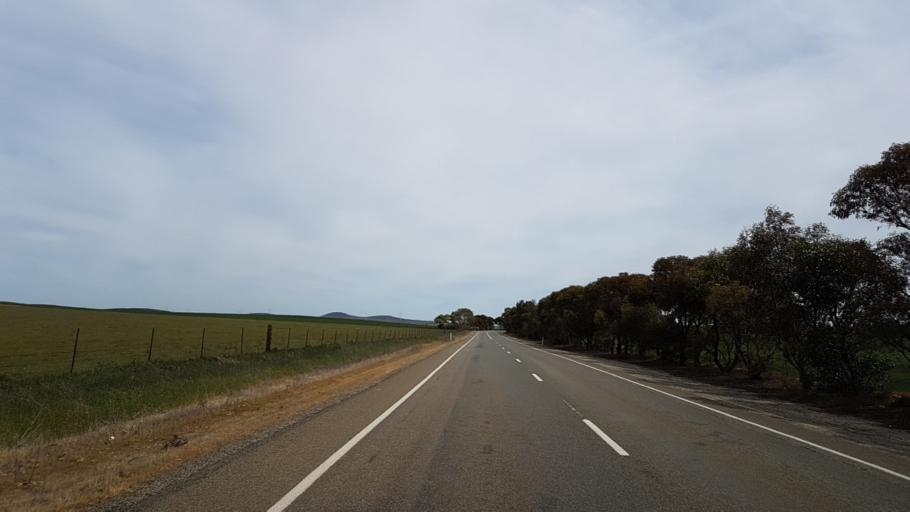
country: AU
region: South Australia
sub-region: Northern Areas
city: Jamestown
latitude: -33.0336
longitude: 138.6560
